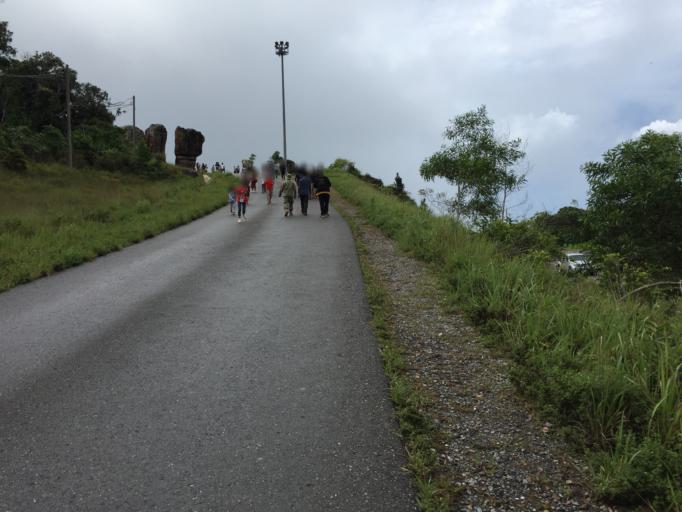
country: KH
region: Kampot
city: Kampot
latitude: 10.6215
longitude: 104.0755
